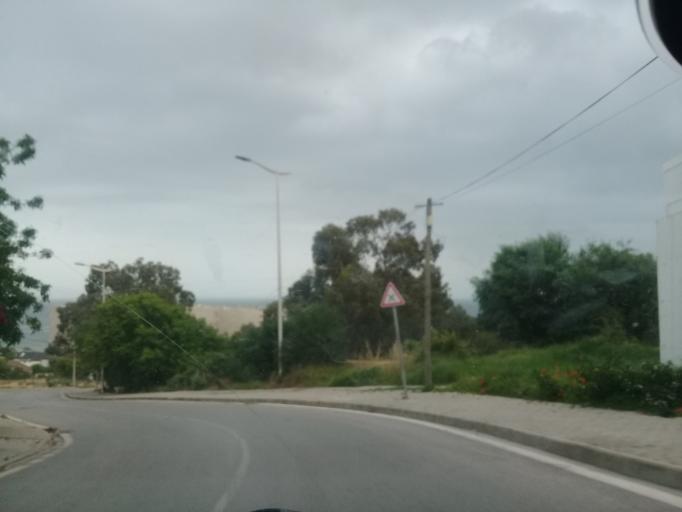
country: TN
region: Tunis
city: Sidi Bou Said
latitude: 36.8663
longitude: 10.3385
